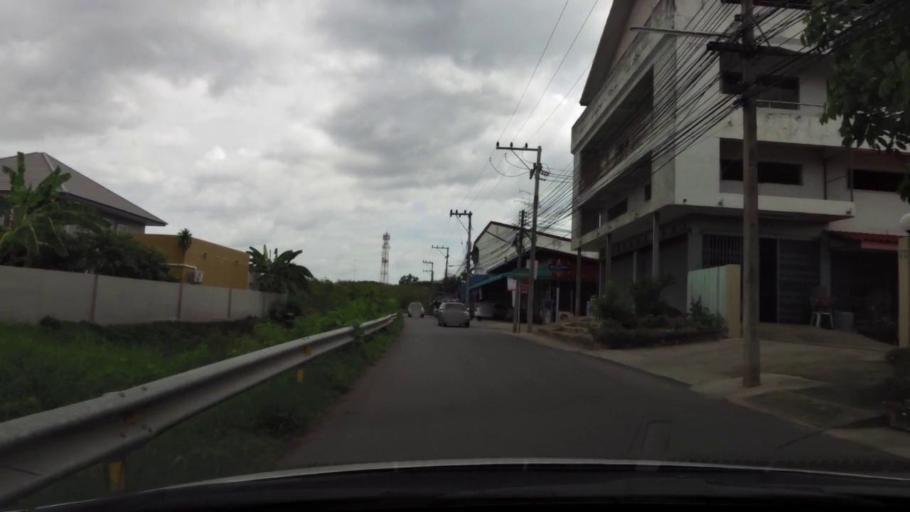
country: TH
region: Ratchaburi
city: Ratchaburi
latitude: 13.5303
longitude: 99.8326
